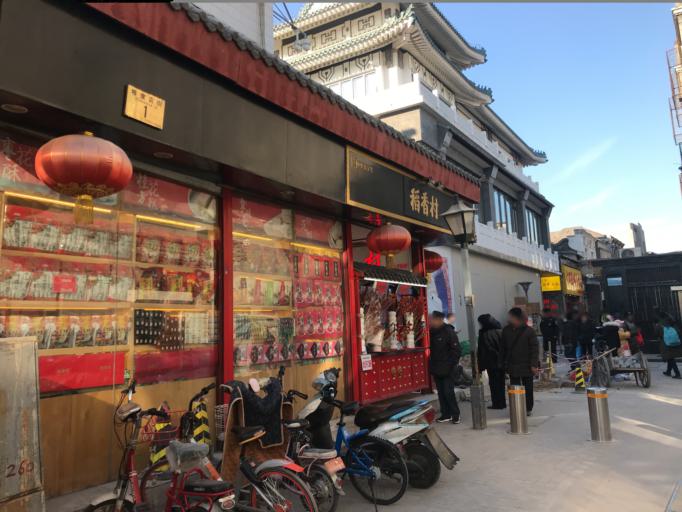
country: CN
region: Beijing
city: Beijing
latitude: 39.8945
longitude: 116.3916
